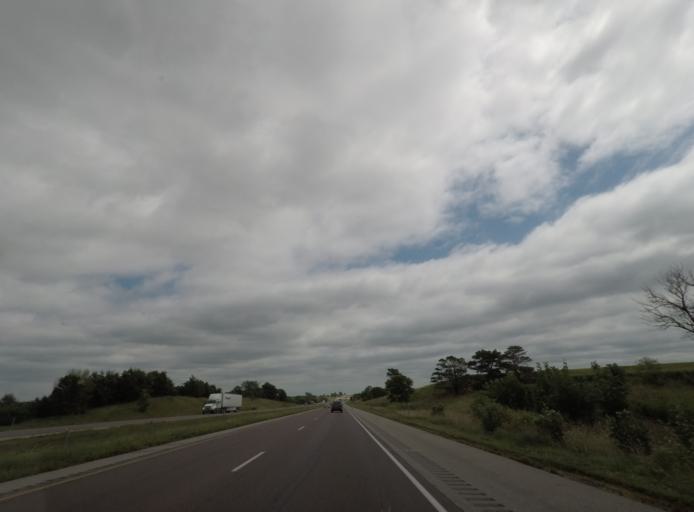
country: US
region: Iowa
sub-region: Poweshiek County
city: Montezuma
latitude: 41.6961
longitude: -92.5713
